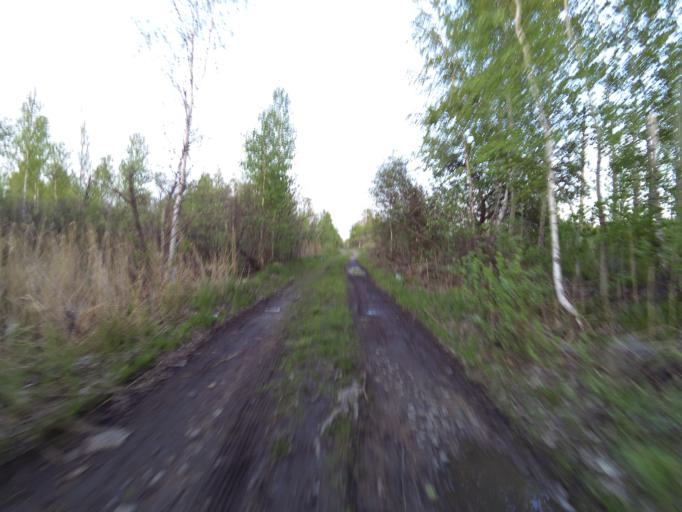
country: RU
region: Sverdlovsk
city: Shirokaya Rechka
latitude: 56.8405
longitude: 60.5057
